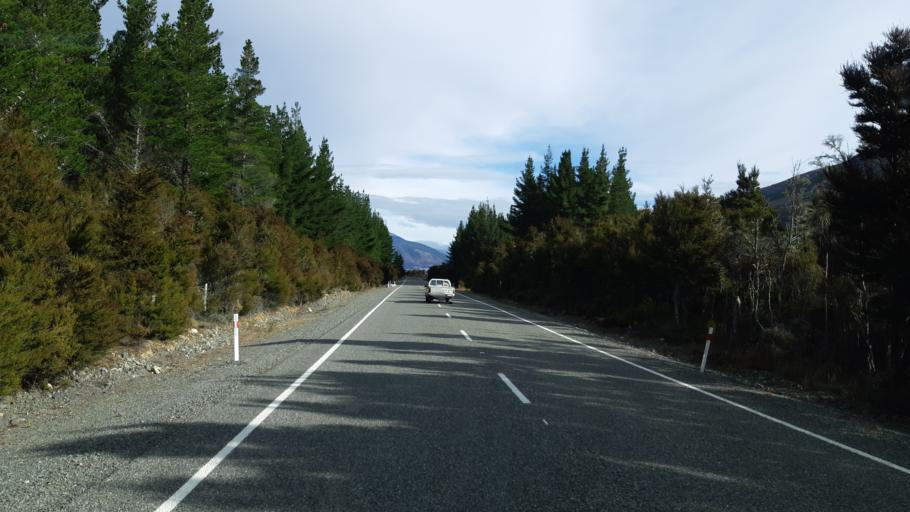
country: NZ
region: Tasman
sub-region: Tasman District
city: Wakefield
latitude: -41.7243
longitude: 173.0529
